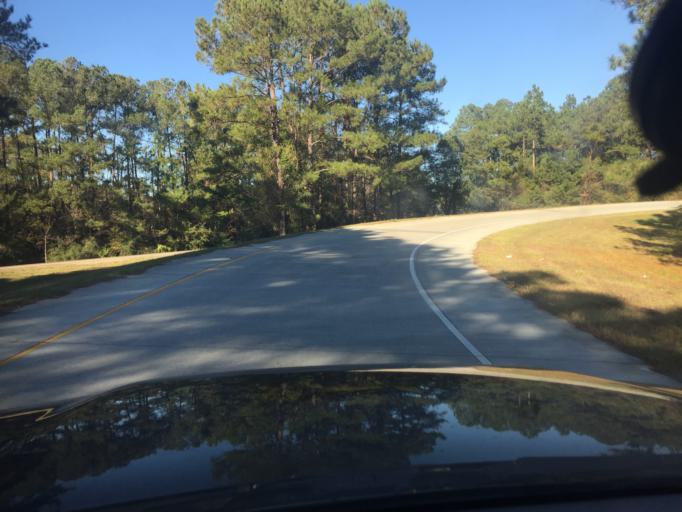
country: US
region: Louisiana
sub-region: Saint Tammany Parish
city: Slidell
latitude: 30.3055
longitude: -89.7429
